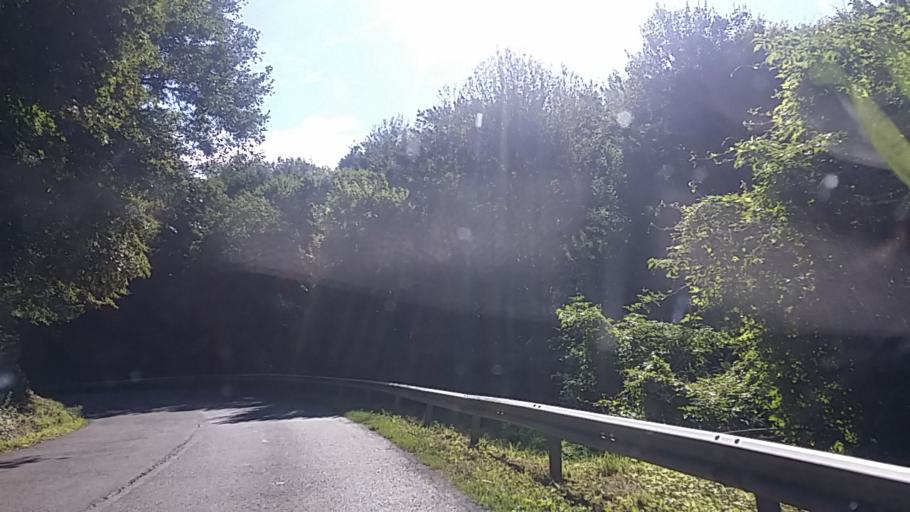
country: HU
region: Baranya
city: Pellerd
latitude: 46.1374
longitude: 18.1272
